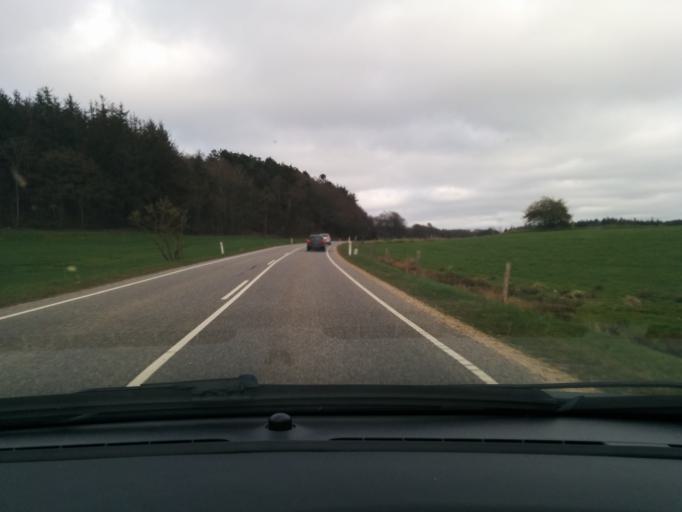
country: DK
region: Central Jutland
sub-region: Favrskov Kommune
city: Hammel
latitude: 56.2153
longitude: 9.7623
